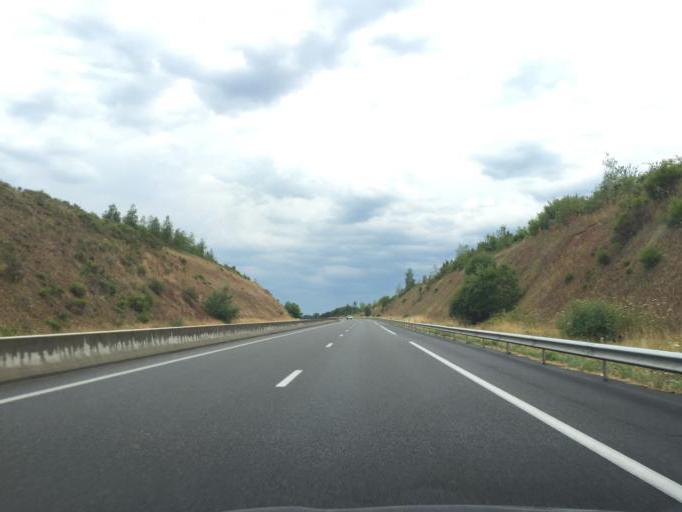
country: FR
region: Auvergne
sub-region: Departement de l'Allier
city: Lapalisse
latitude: 46.2289
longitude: 3.6497
